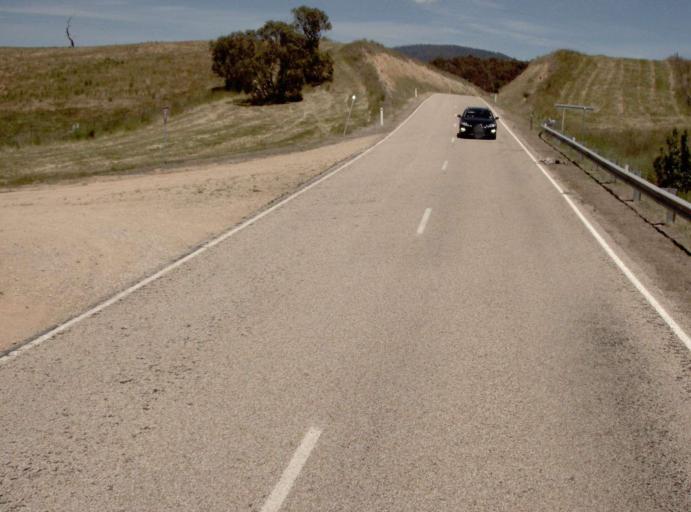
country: AU
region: Victoria
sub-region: Alpine
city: Mount Beauty
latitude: -37.1214
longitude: 147.6288
